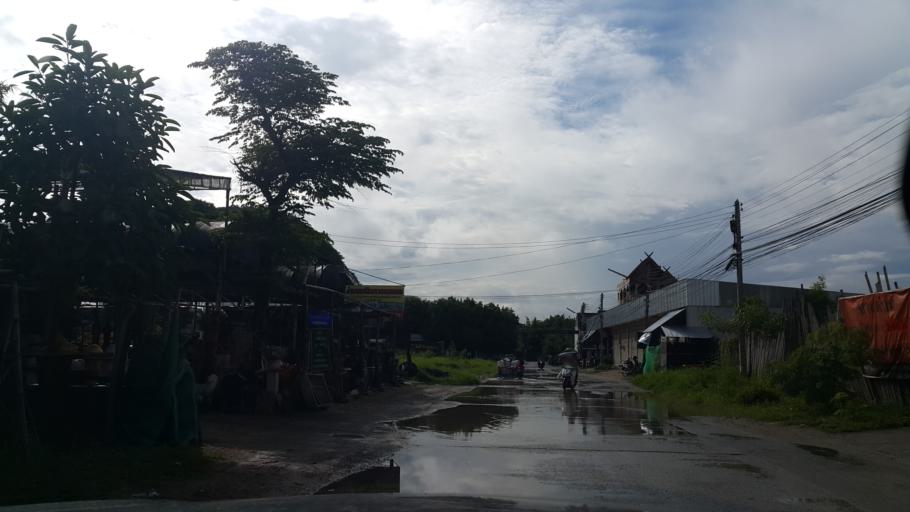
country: TH
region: Chiang Mai
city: Chiang Mai
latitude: 18.8032
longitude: 98.9985
